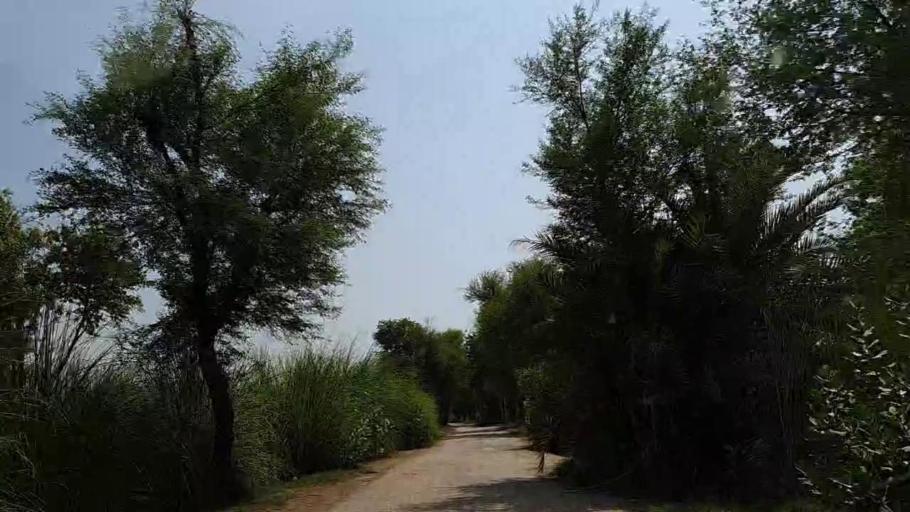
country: PK
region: Sindh
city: Adilpur
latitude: 27.9083
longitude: 69.3643
